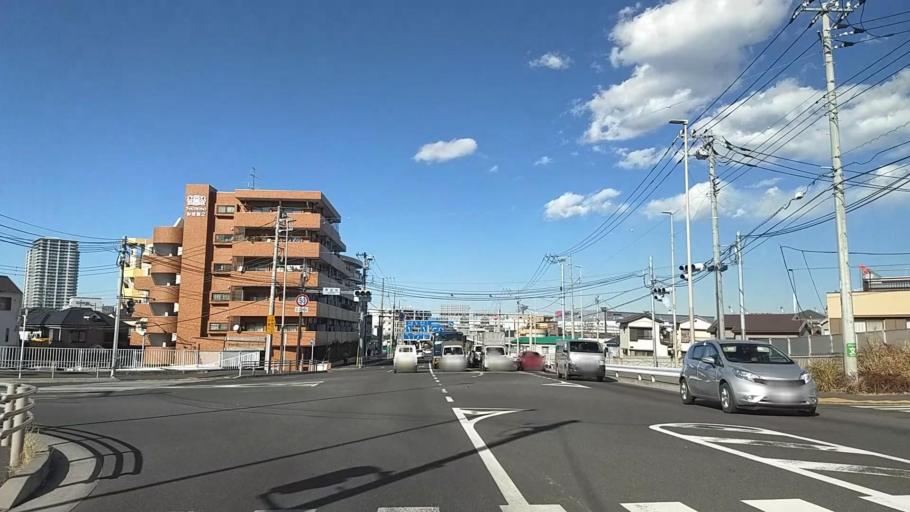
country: JP
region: Kanagawa
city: Yokohama
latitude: 35.3790
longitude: 139.6220
